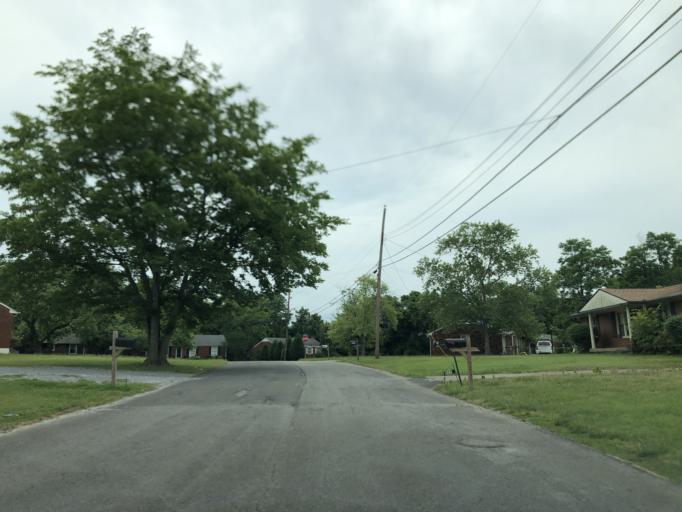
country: US
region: Tennessee
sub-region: Davidson County
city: Goodlettsville
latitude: 36.2894
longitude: -86.7137
